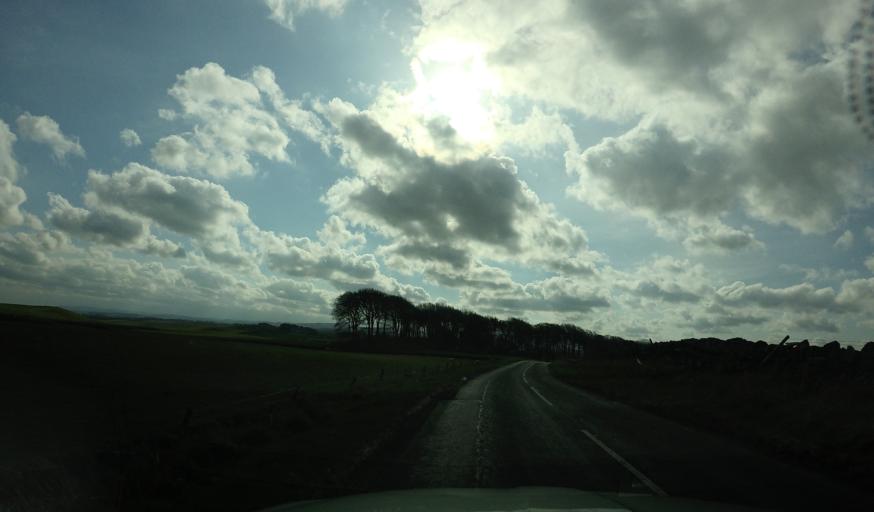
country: GB
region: Scotland
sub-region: Midlothian
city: Penicuik
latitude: 55.8043
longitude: -3.1746
